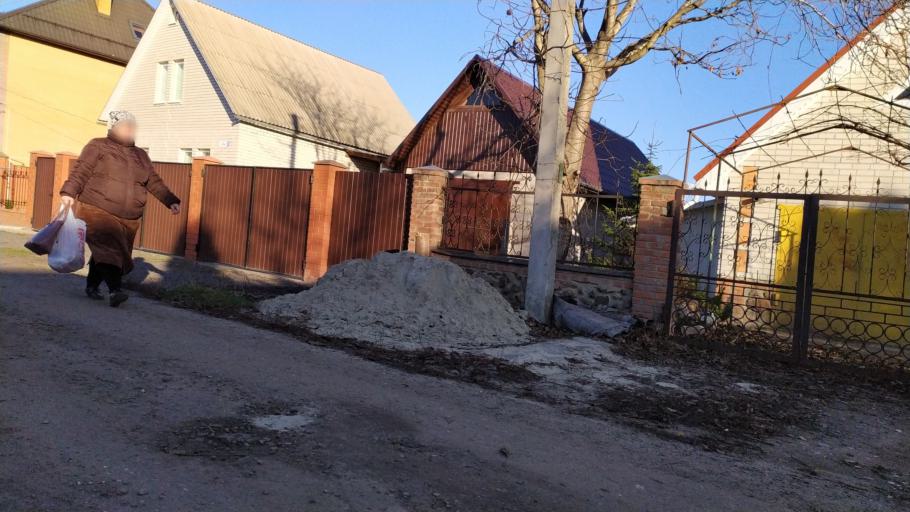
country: RU
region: Kursk
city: Kursk
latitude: 51.6458
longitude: 36.1379
